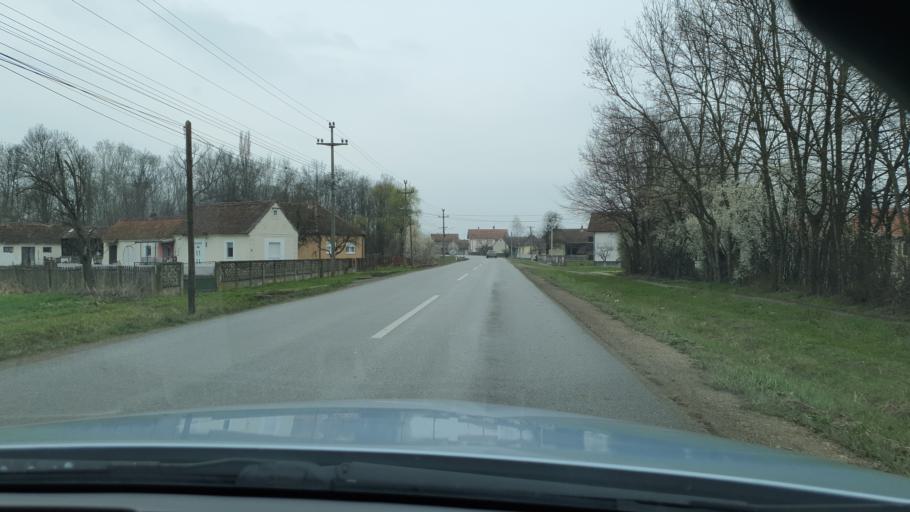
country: RS
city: Belotic
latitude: 44.8121
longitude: 19.5518
